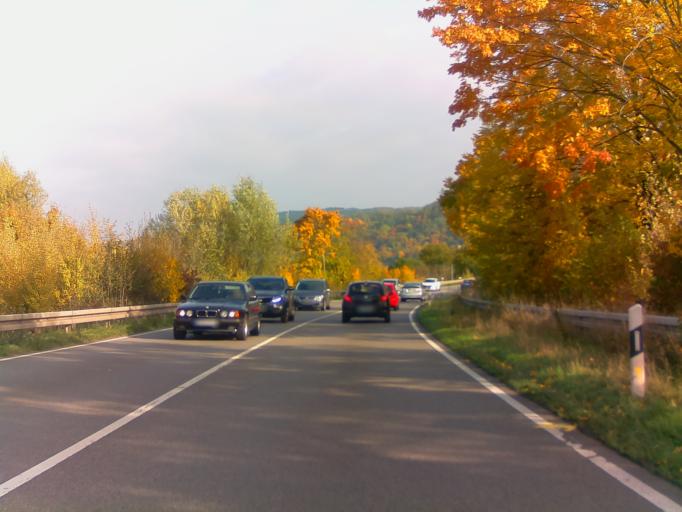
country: DE
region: Baden-Wuerttemberg
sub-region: Karlsruhe Region
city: Weinheim
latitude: 49.5673
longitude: 8.6534
